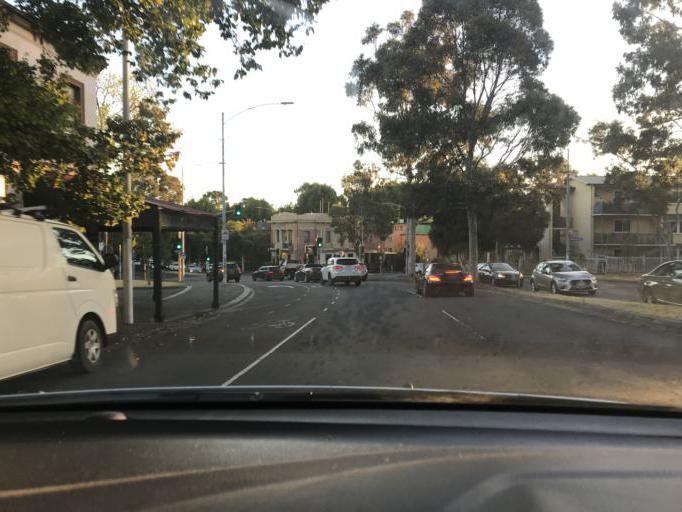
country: AU
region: Victoria
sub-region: Melbourne
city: North Melbourne
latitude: -37.7980
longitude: 144.9494
